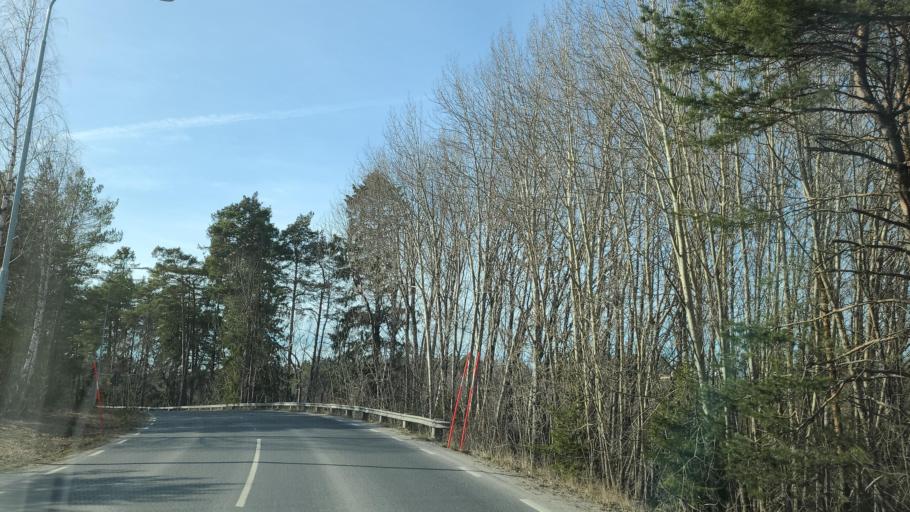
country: SE
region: Stockholm
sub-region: Ekero Kommun
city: Ekeroe
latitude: 59.2820
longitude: 17.7709
